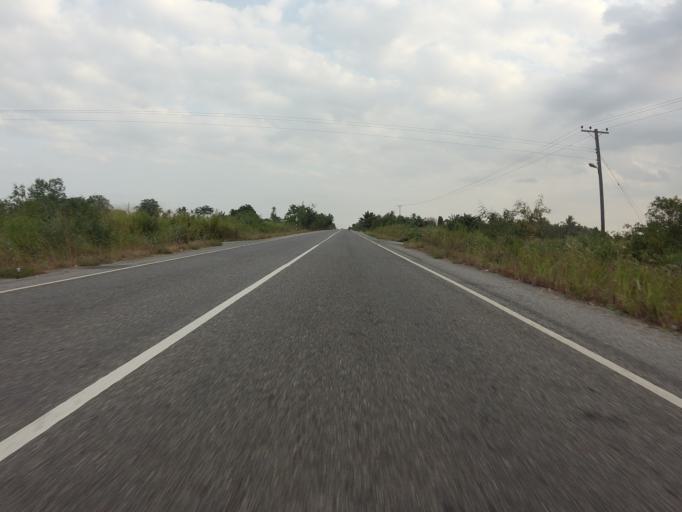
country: GH
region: Volta
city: Ho
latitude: 6.2521
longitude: 0.5507
